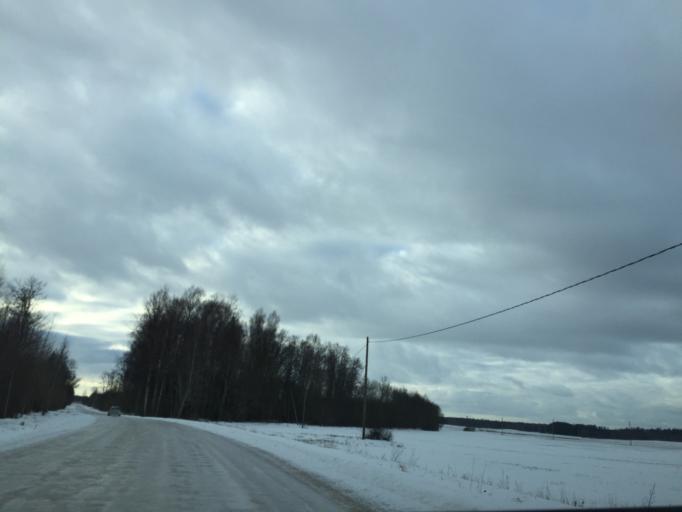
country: LV
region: Lielvarde
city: Lielvarde
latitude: 56.5997
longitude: 24.7423
